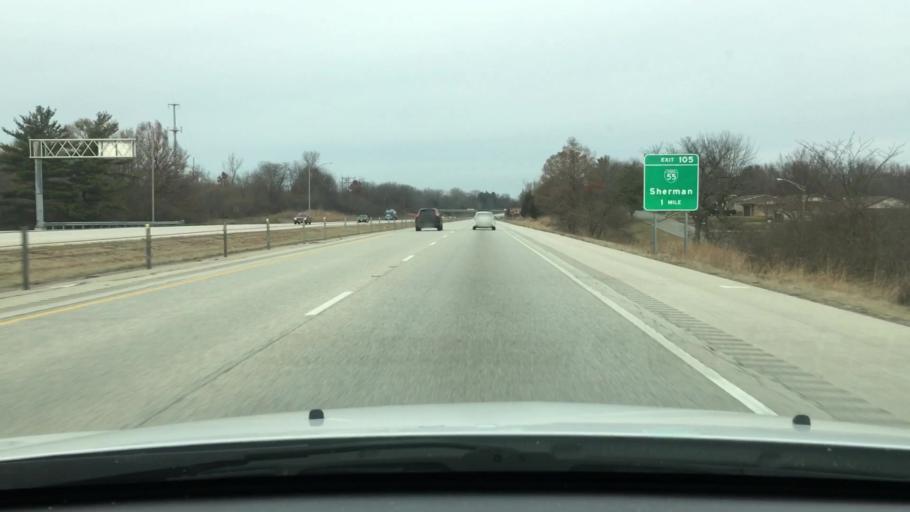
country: US
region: Illinois
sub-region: Sangamon County
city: Sherman
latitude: 39.8892
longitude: -89.5958
